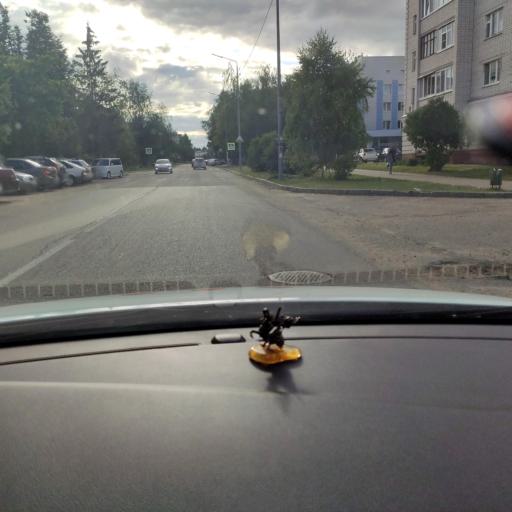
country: RU
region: Tatarstan
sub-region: Zelenodol'skiy Rayon
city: Zelenodolsk
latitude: 55.8511
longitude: 48.4969
